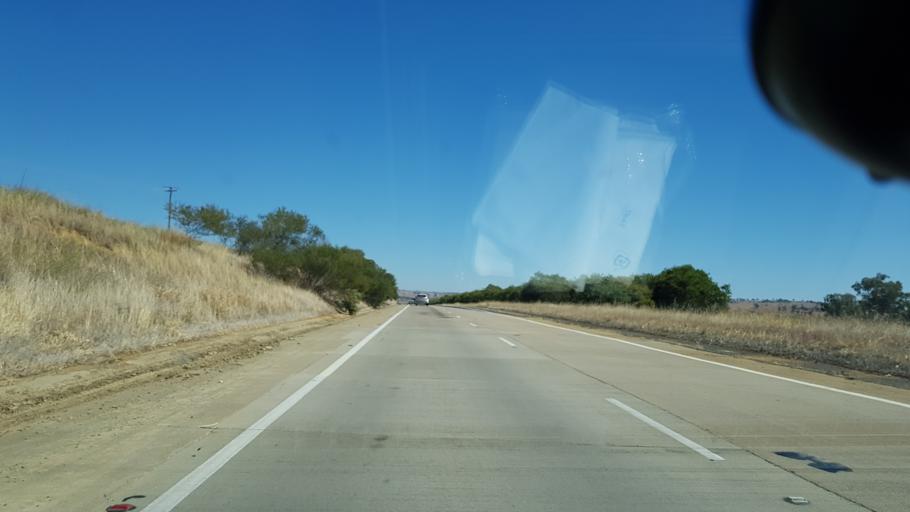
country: AU
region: New South Wales
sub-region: Gundagai
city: Gundagai
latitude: -34.8161
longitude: 148.4005
